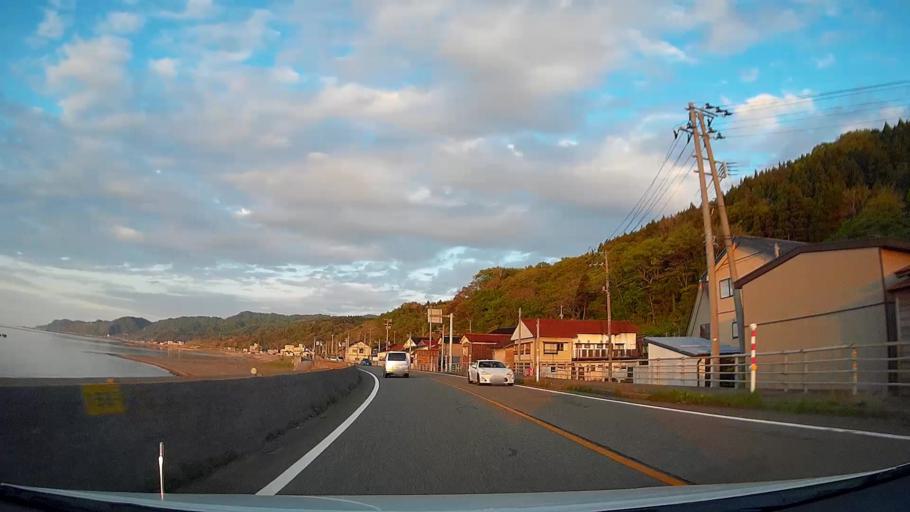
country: JP
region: Niigata
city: Itoigawa
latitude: 37.1141
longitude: 138.0182
